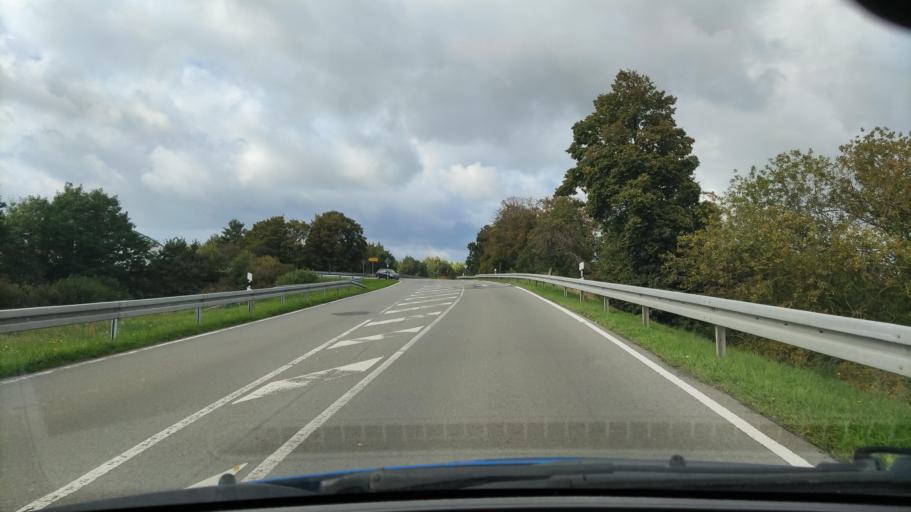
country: DE
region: Saxony-Anhalt
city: Salzwedel
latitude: 52.8550
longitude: 11.1870
